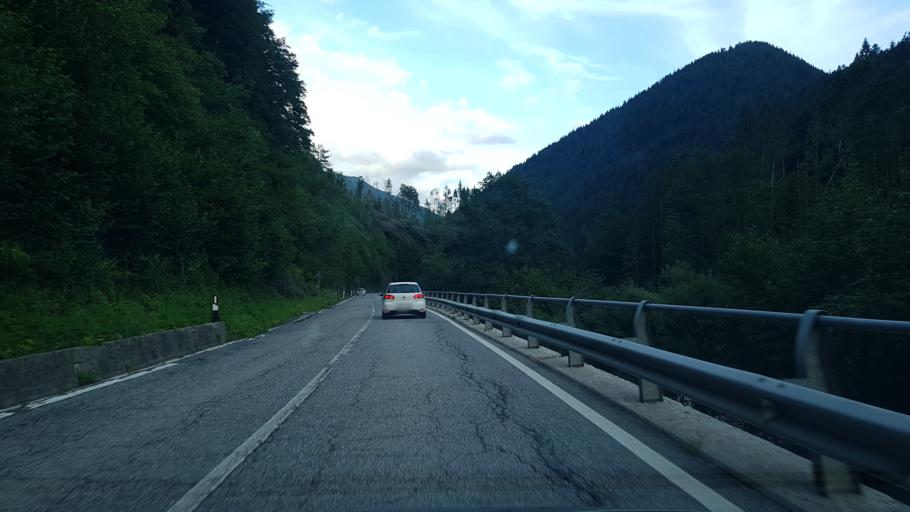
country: IT
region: Friuli Venezia Giulia
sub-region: Provincia di Udine
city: Forni Avoltri
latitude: 46.5721
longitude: 12.8055
